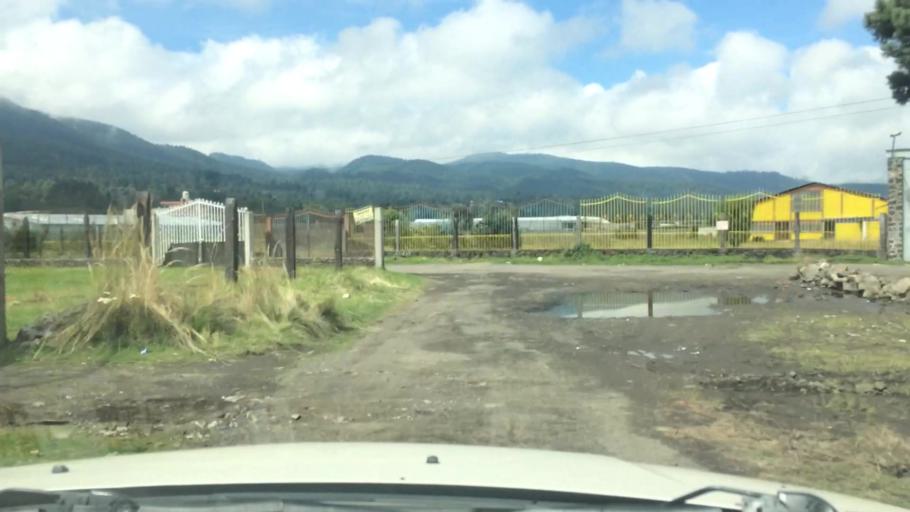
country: MX
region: Mexico City
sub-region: Tlalpan
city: Lomas de Tepemecatl
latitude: 19.2330
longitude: -99.2247
